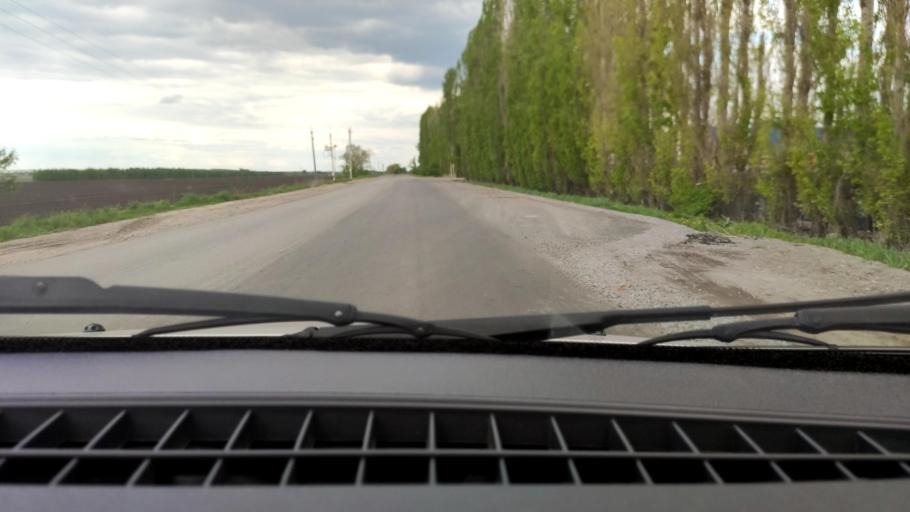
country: RU
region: Voronezj
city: Podkletnoye
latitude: 51.5900
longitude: 39.4750
